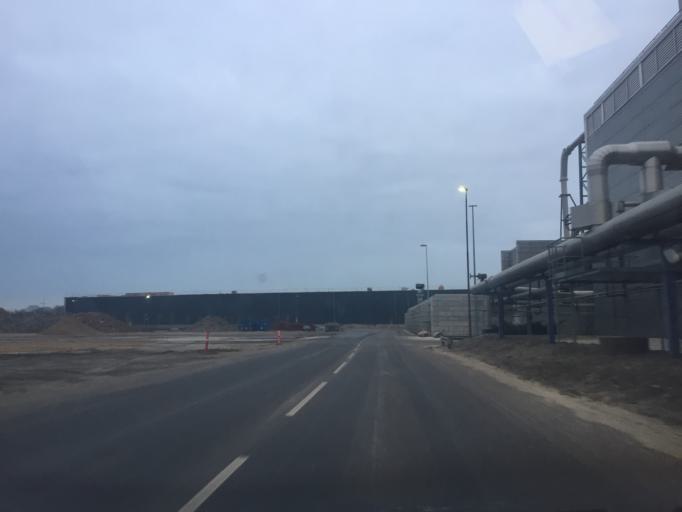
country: DK
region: Zealand
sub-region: Koge Kommune
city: Koge
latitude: 55.4630
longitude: 12.1919
